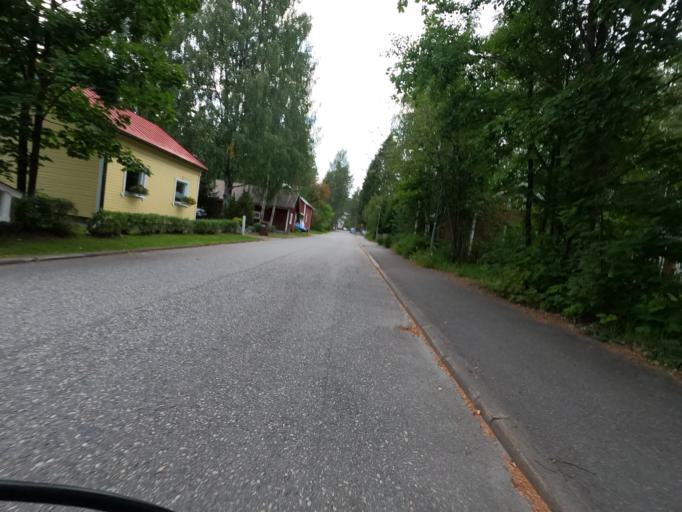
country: FI
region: North Karelia
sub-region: Joensuu
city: Joensuu
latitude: 62.6112
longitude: 29.8297
